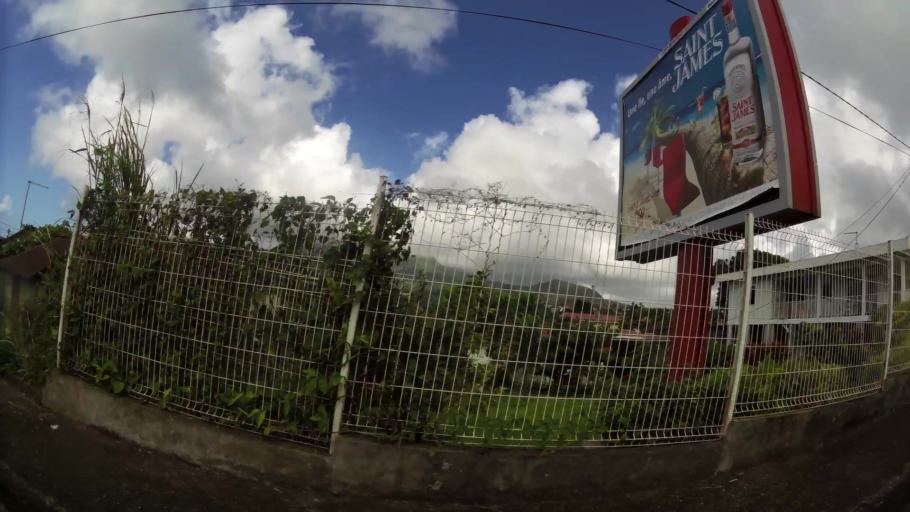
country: MQ
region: Martinique
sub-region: Martinique
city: Le Morne-Rouge
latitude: 14.7708
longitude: -61.1385
